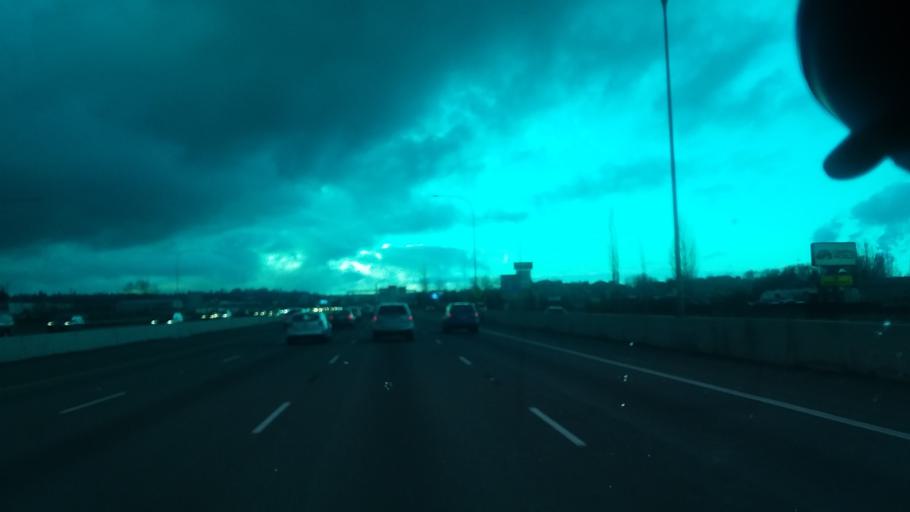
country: US
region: Washington
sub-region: Pierce County
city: Fife
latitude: 47.2397
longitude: -122.3629
